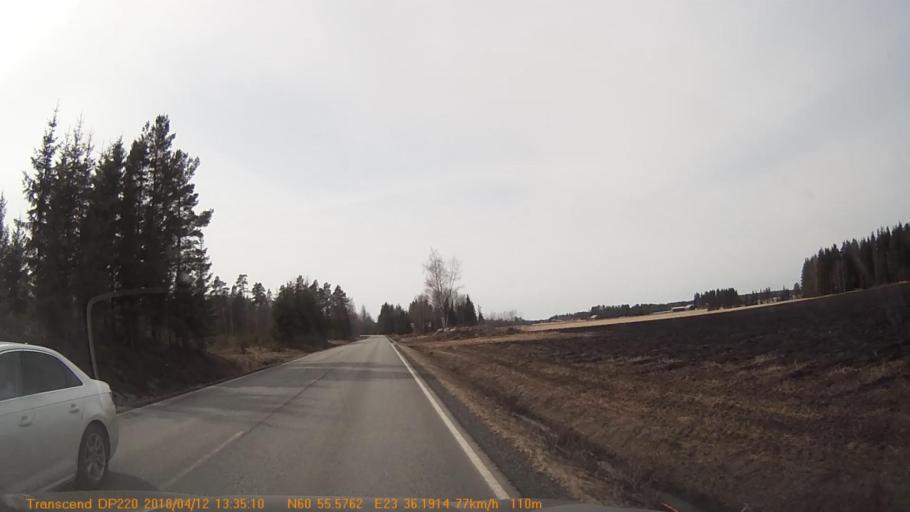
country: FI
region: Haeme
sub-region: Forssa
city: Forssa
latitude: 60.9262
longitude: 23.6025
